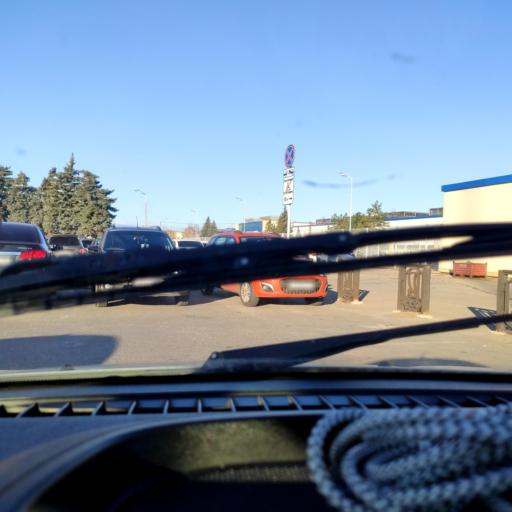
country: RU
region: Samara
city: Tol'yatti
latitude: 53.5574
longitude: 49.2532
